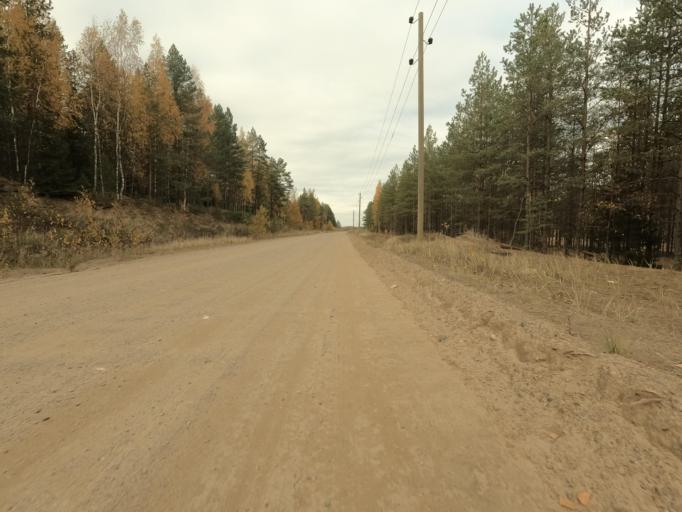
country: RU
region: Leningrad
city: Priladozhskiy
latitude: 59.6967
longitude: 31.3618
